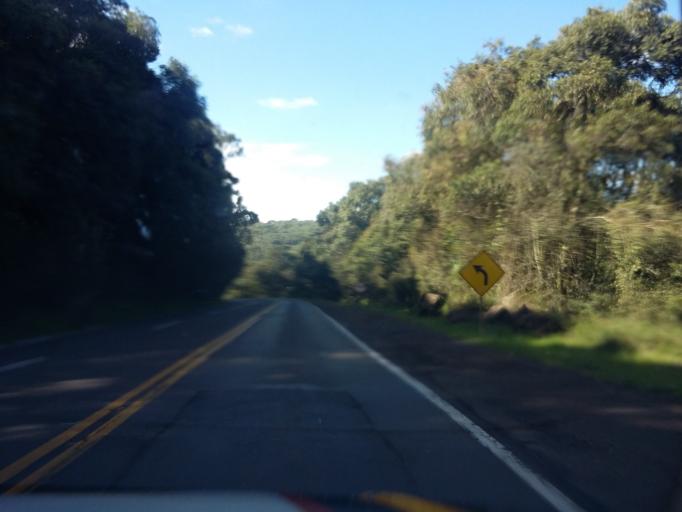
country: BR
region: Rio Grande do Sul
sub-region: Vacaria
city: Vacaria
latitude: -28.5772
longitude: -51.0173
